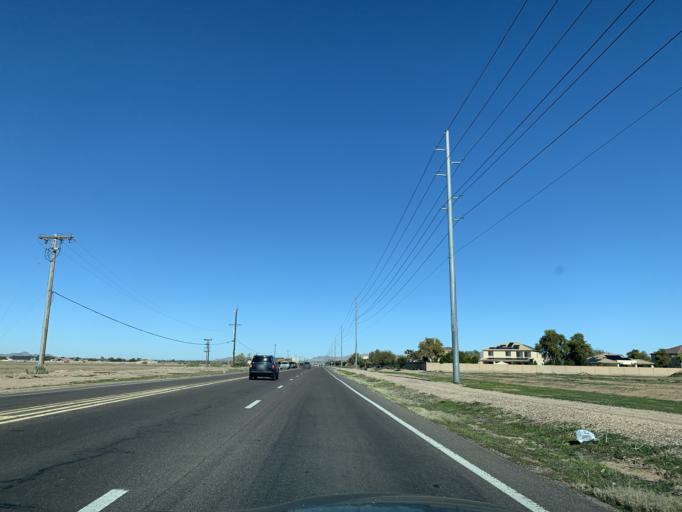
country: US
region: Arizona
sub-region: Pinal County
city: Casa Grande
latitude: 32.8967
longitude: -111.7226
